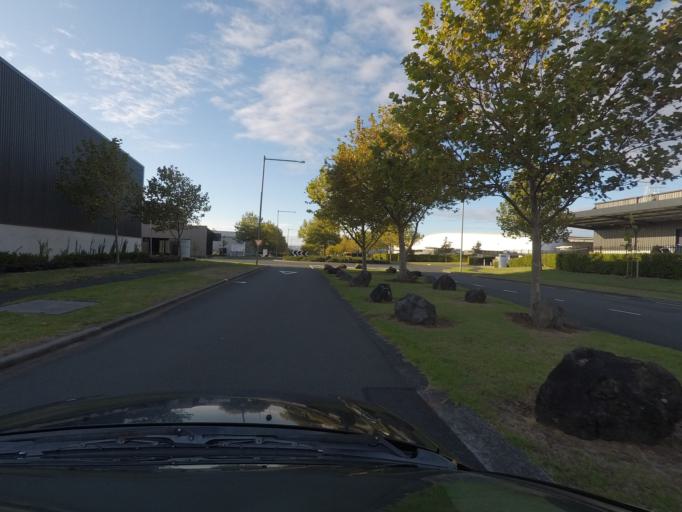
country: NZ
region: Auckland
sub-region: Auckland
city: Manukau City
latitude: -36.9399
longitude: 174.8748
